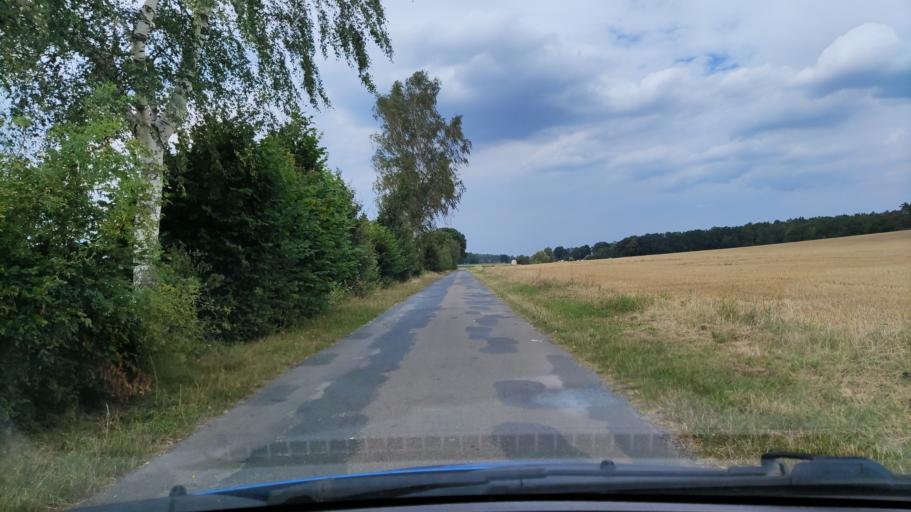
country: DE
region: Lower Saxony
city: Schnega
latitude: 52.9319
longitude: 10.8805
